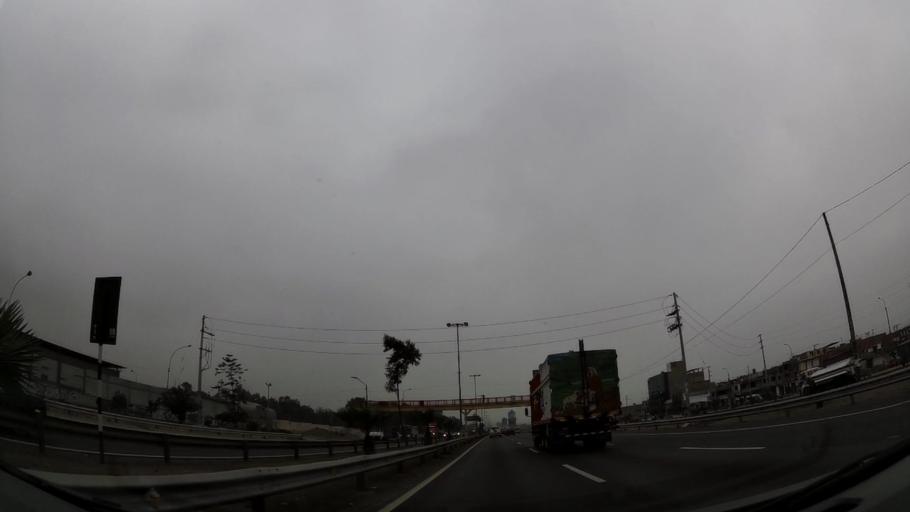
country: PE
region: Lima
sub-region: Lima
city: Surco
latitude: -12.1792
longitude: -76.9766
